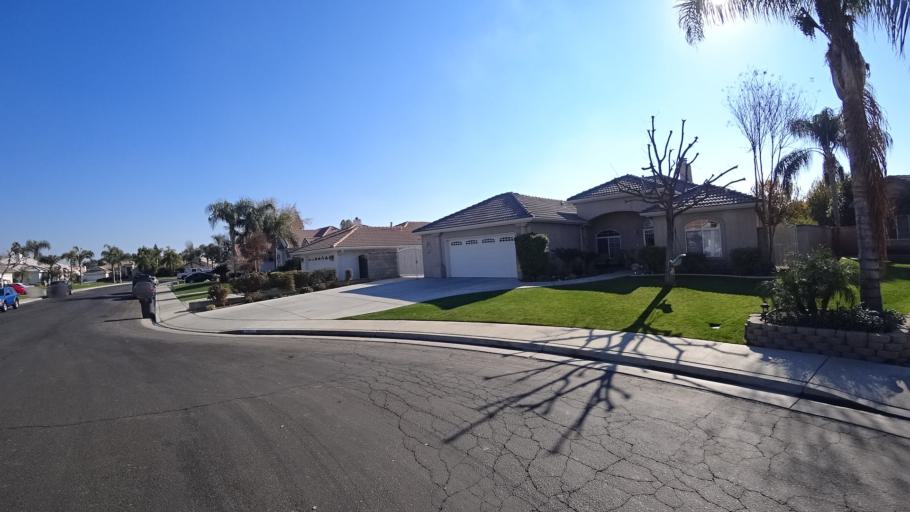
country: US
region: California
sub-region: Kern County
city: Greenfield
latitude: 35.3009
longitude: -119.0608
